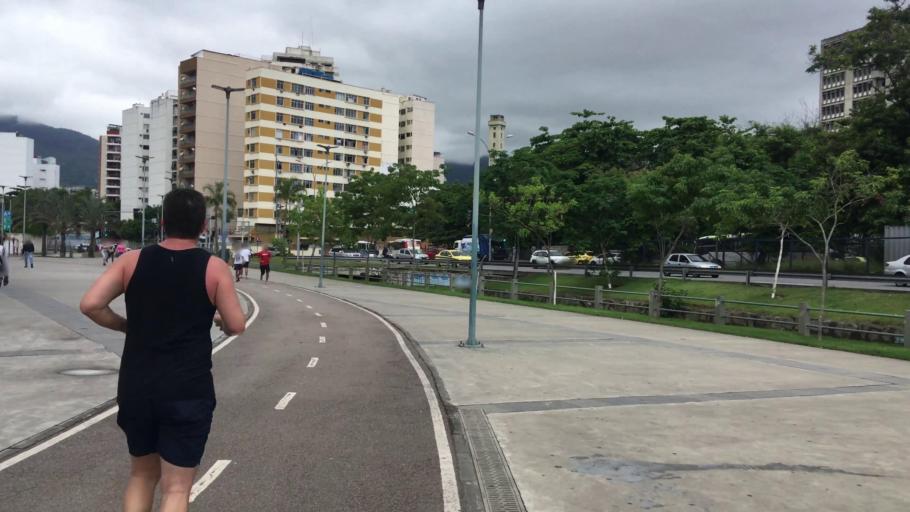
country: BR
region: Rio de Janeiro
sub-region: Rio De Janeiro
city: Rio de Janeiro
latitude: -22.9112
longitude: -43.2334
